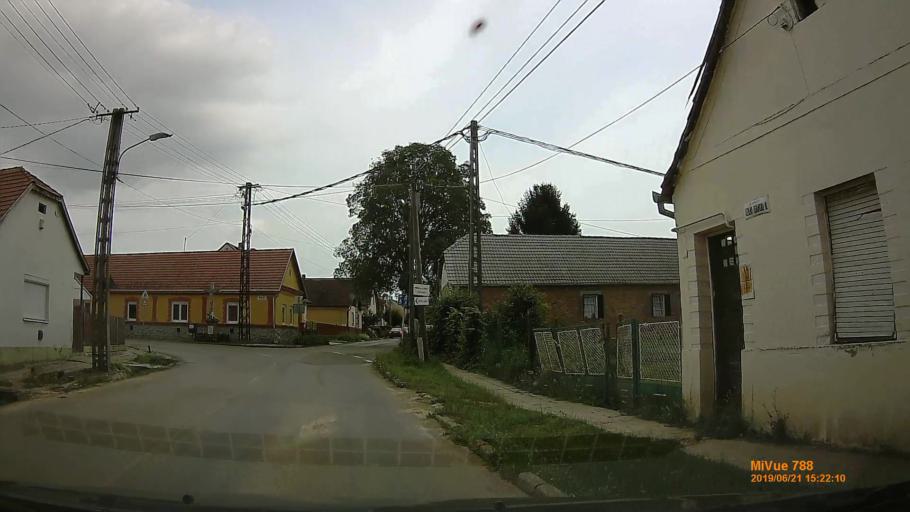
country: HU
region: Baranya
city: Pecs
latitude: 46.0432
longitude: 18.2503
